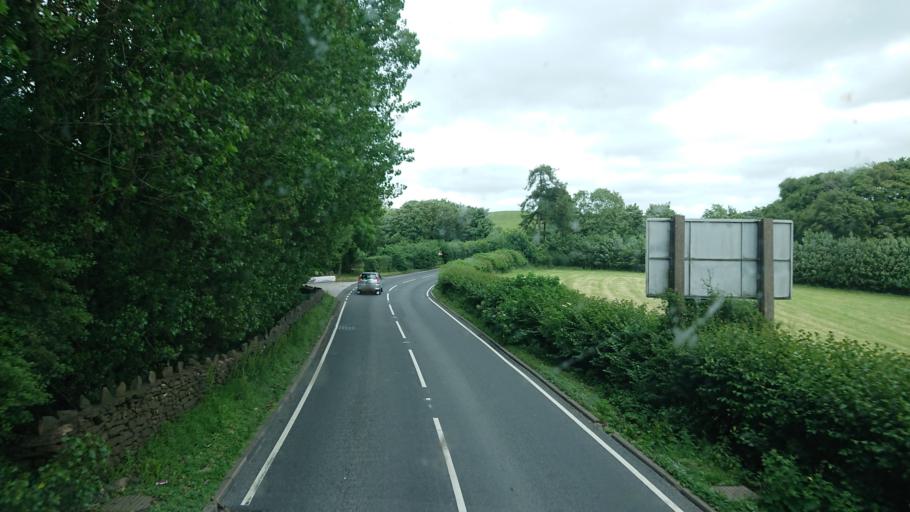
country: GB
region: England
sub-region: Cumbria
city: Milnthorpe
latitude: 54.2361
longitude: -2.7113
